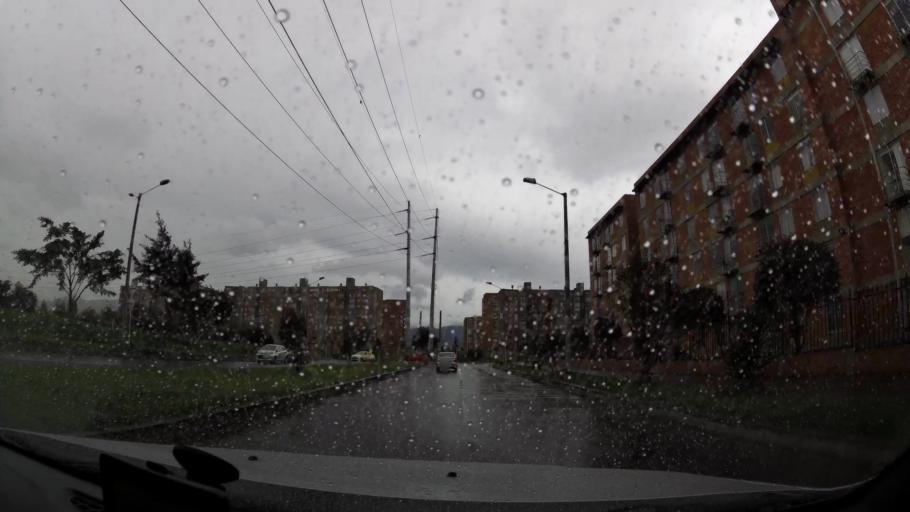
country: CO
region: Bogota D.C.
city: Bogota
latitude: 4.6592
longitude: -74.1304
